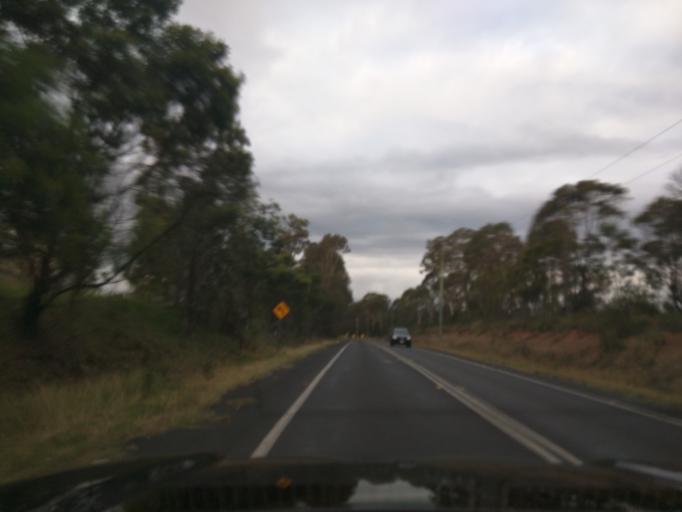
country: AU
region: New South Wales
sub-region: Wollondilly
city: Douglas Park
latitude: -34.2213
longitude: 150.7655
